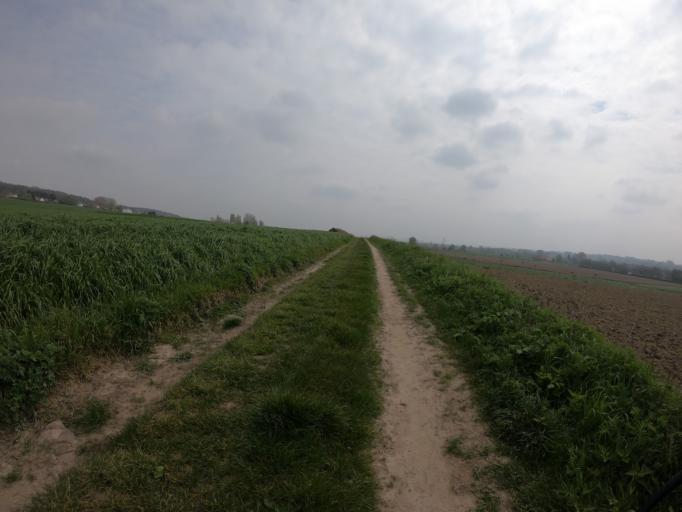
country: BE
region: Wallonia
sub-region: Province du Hainaut
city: Celles
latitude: 50.7497
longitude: 3.4847
